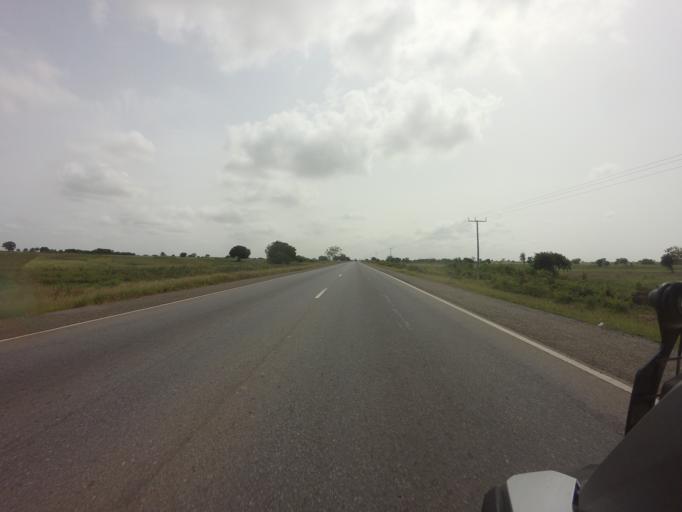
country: GH
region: Volta
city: Anloga
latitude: 5.8856
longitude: 0.4414
